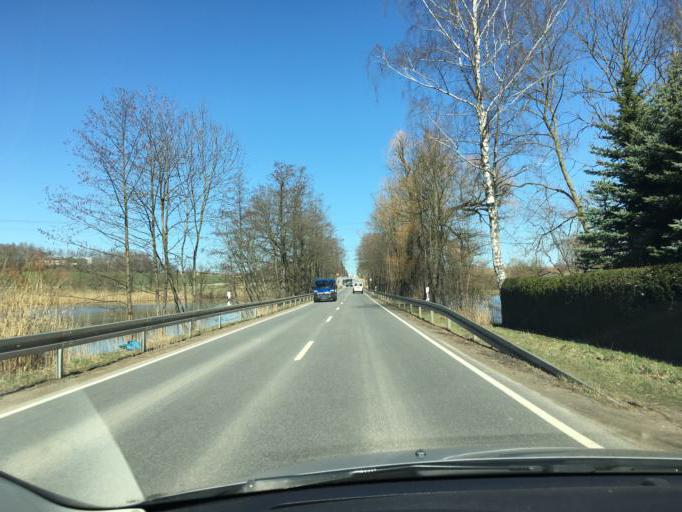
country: DE
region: Saxony
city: Limbach-Oberfrohna
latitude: 50.8729
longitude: 12.7789
